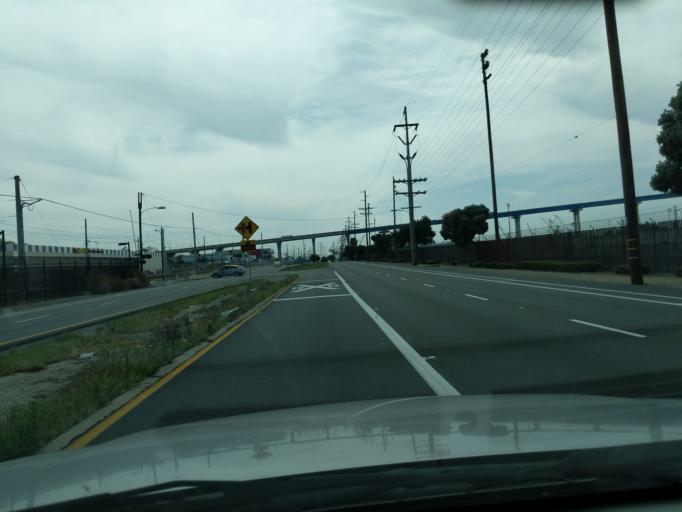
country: US
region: California
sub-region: San Diego County
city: San Diego
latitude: 32.7009
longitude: -117.1514
